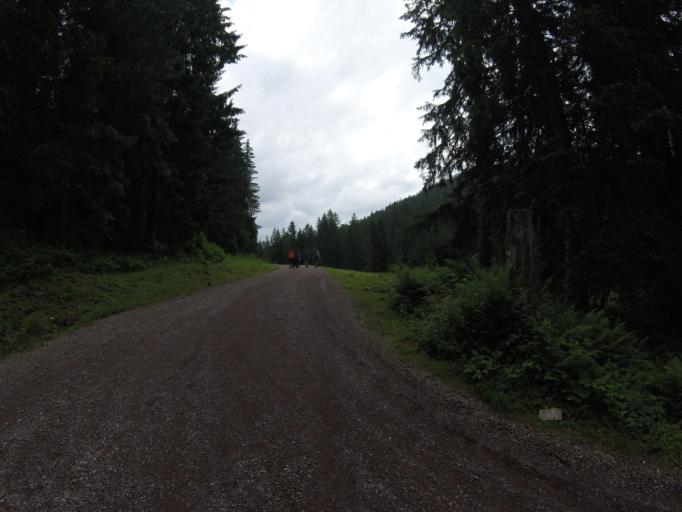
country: AT
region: Tyrol
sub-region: Politischer Bezirk Kitzbuhel
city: Waidring
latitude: 47.6532
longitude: 12.6036
